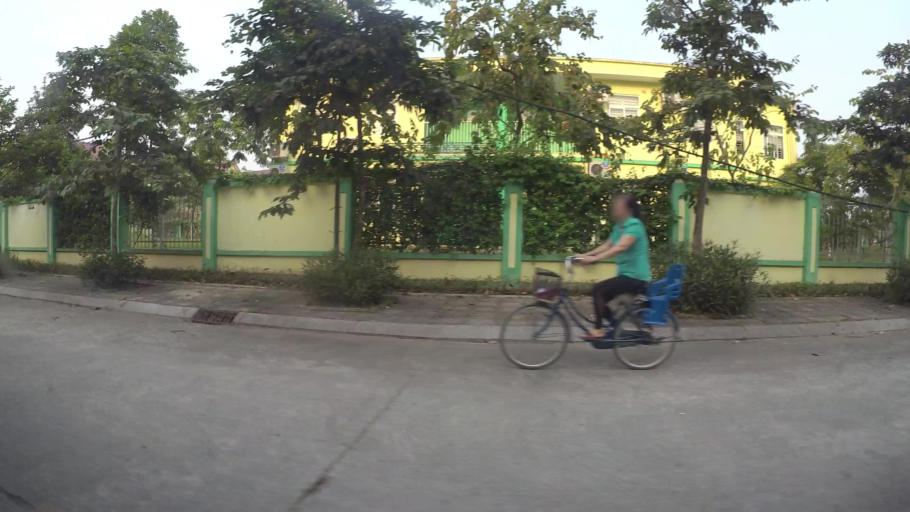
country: VN
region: Ha Noi
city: Cau Dien
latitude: 21.0067
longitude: 105.7329
